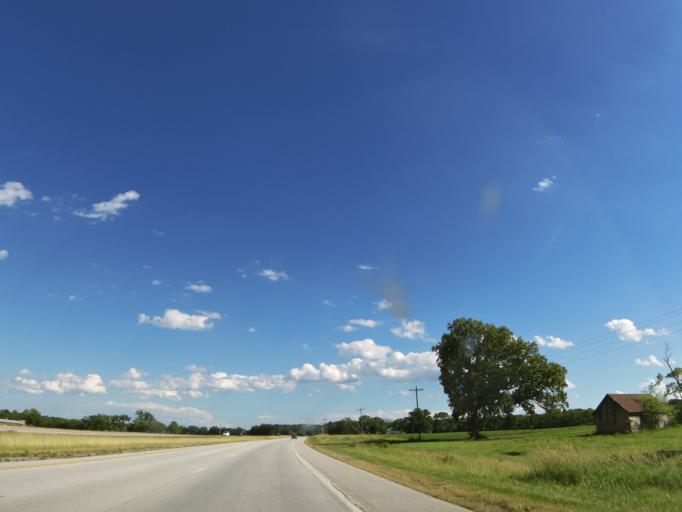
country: US
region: Illinois
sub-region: Hancock County
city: Warsaw
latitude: 40.2550
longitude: -91.5447
